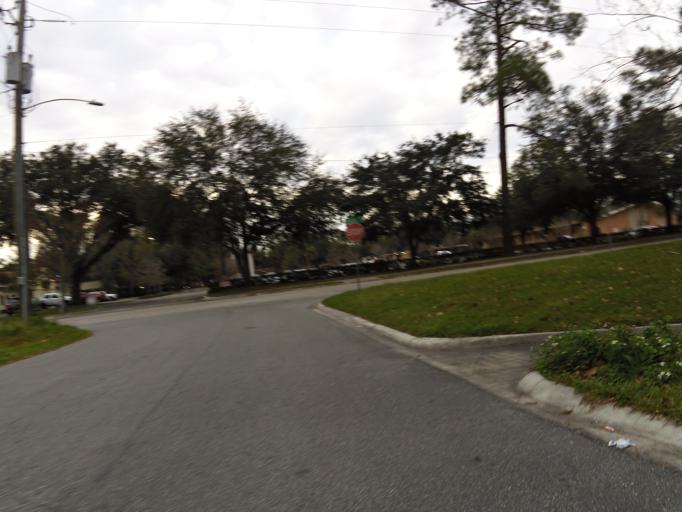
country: US
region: Florida
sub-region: Duval County
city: Jacksonville
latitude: 30.2471
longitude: -81.6246
